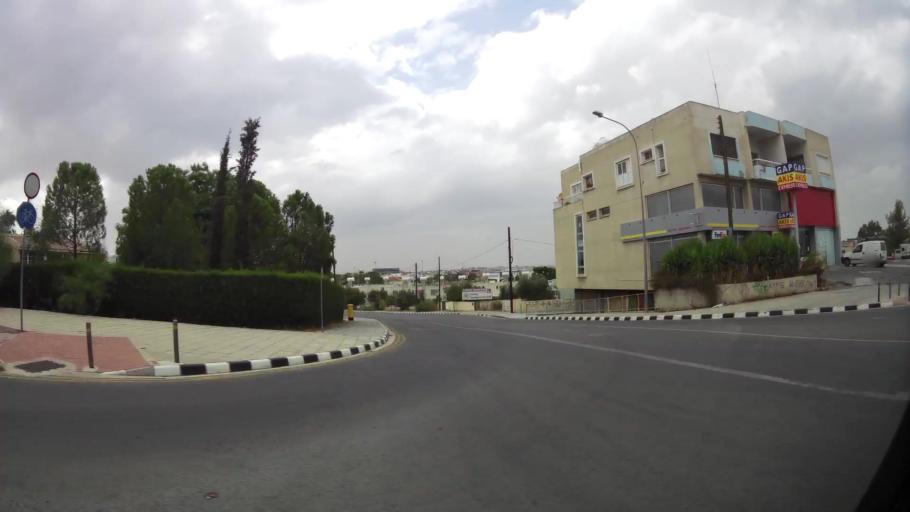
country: CY
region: Lefkosia
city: Geri
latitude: 35.1136
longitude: 33.3769
